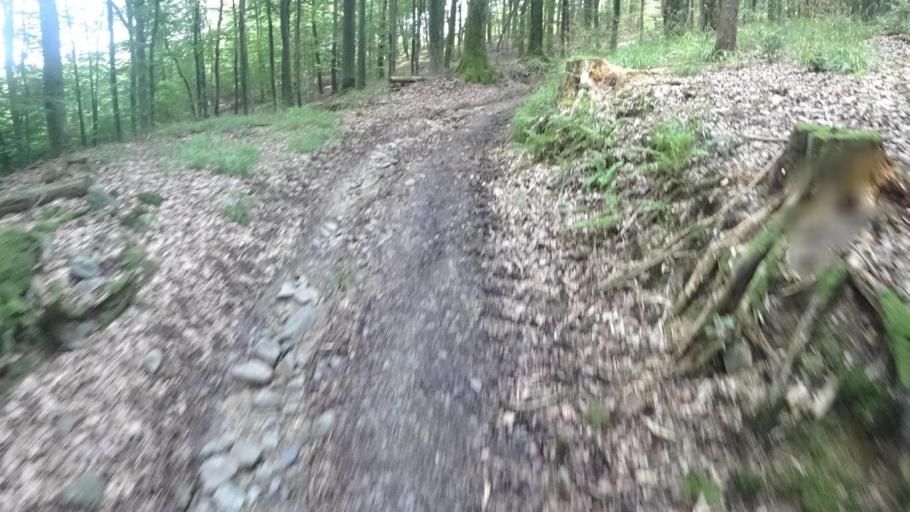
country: DE
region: Rheinland-Pfalz
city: Sankt Katharinen
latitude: 50.5734
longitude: 7.3612
